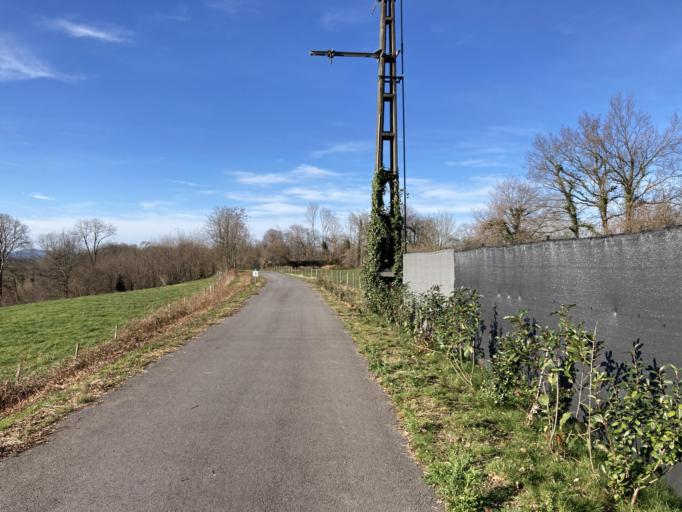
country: FR
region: Aquitaine
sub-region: Departement des Pyrenees-Atlantiques
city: Arudy
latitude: 43.1412
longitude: -0.4506
